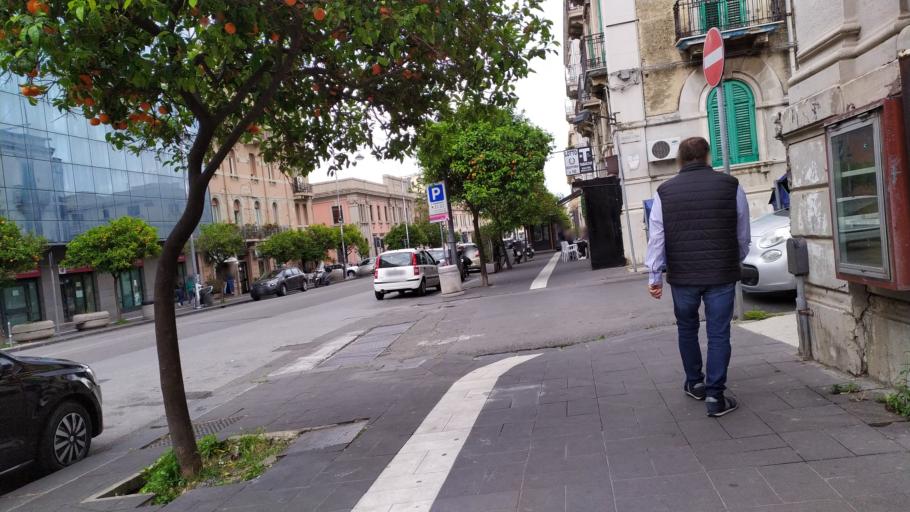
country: IT
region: Sicily
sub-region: Messina
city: Messina
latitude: 38.1880
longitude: 15.5540
